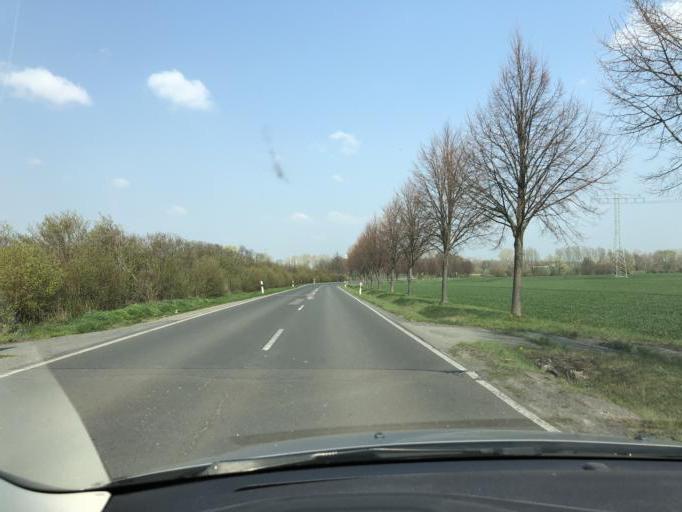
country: DE
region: Saxony
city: Rackwitz
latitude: 51.4315
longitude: 12.3864
